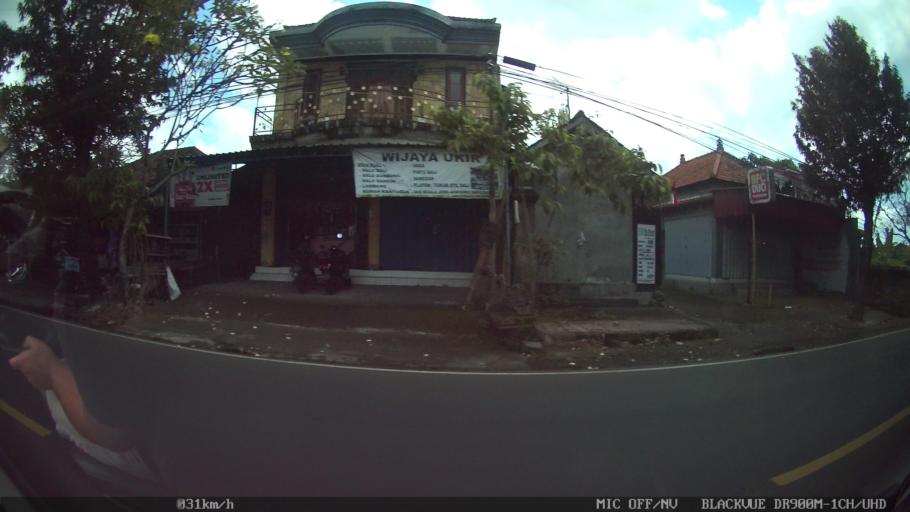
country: ID
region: Bali
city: Banjar Sedang
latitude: -8.5656
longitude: 115.2868
